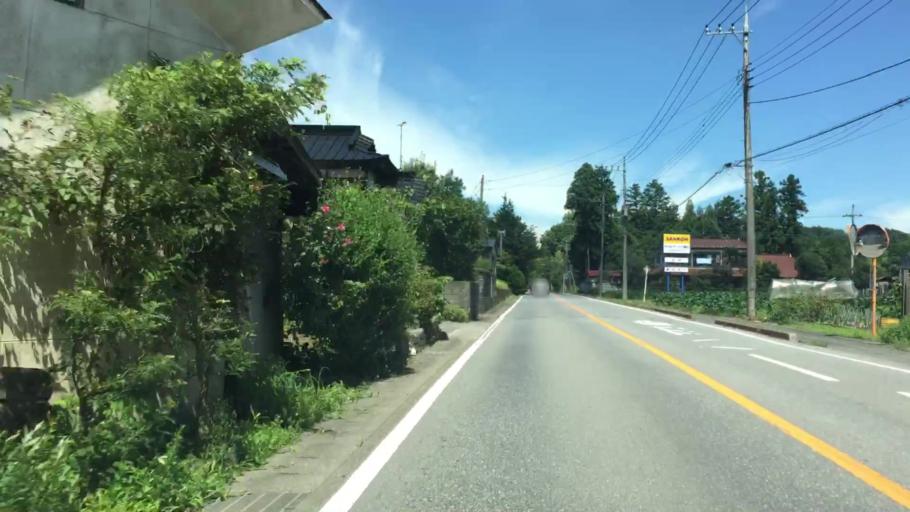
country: JP
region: Tochigi
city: Imaichi
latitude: 36.7148
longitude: 139.7519
